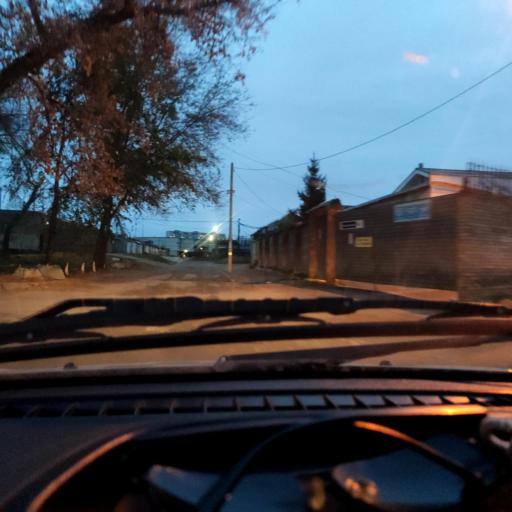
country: RU
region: Samara
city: Tol'yatti
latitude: 53.5136
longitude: 49.4374
